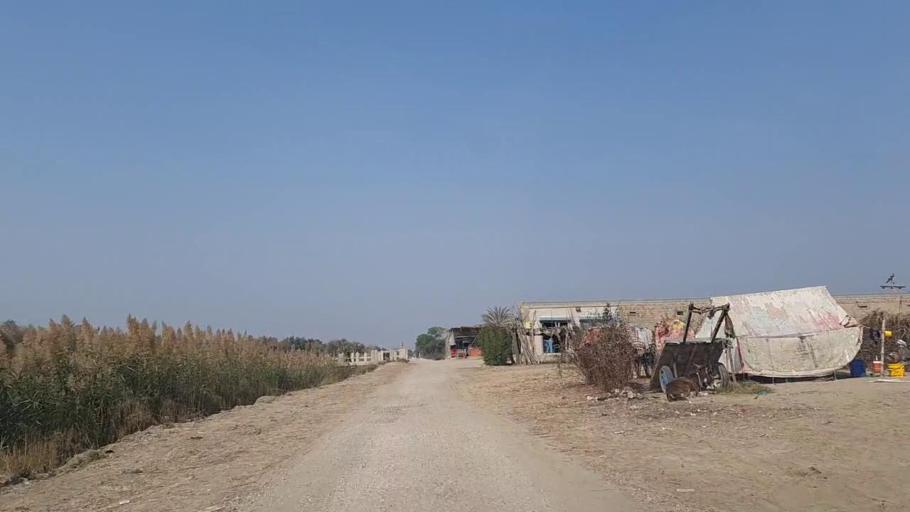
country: PK
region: Sindh
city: Daur
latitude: 26.4751
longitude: 68.4658
